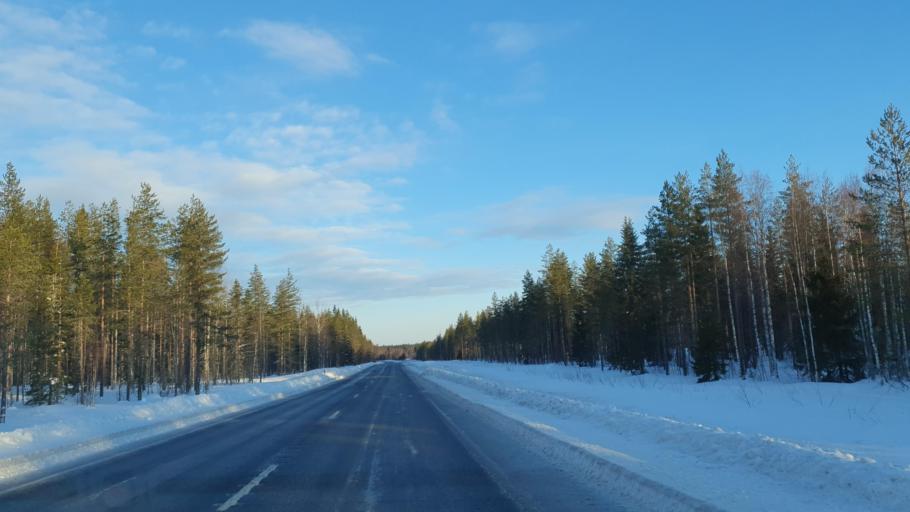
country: FI
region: Kainuu
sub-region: Kajaani
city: Vuolijoki
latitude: 64.5205
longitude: 27.2764
